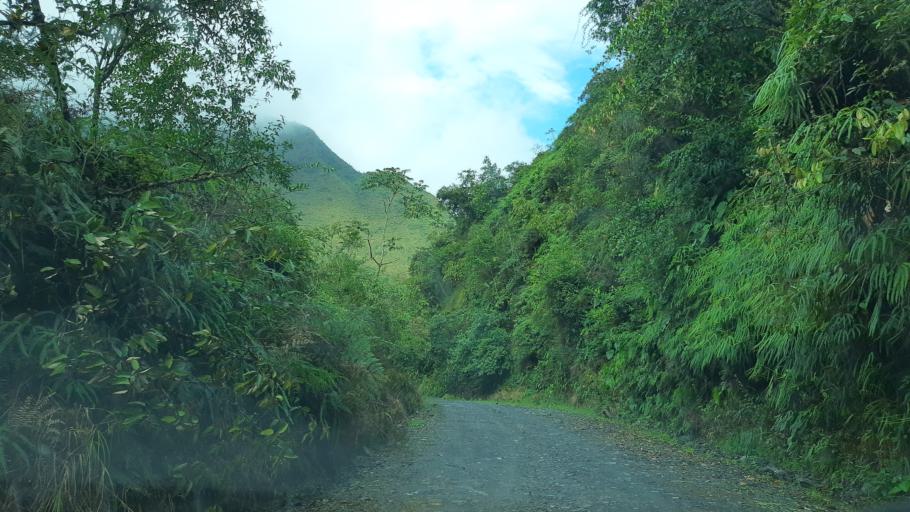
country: CO
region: Boyaca
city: Chivor
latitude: 4.9122
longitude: -73.3074
